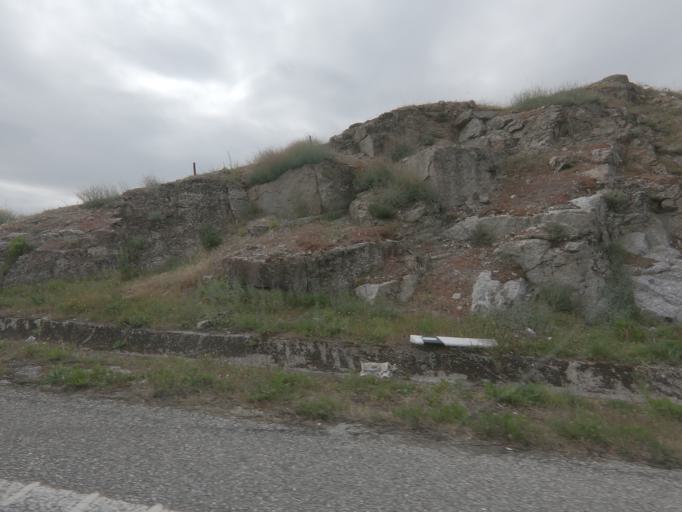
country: PT
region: Guarda
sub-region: Guarda
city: Guarda
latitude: 40.6141
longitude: -7.2831
